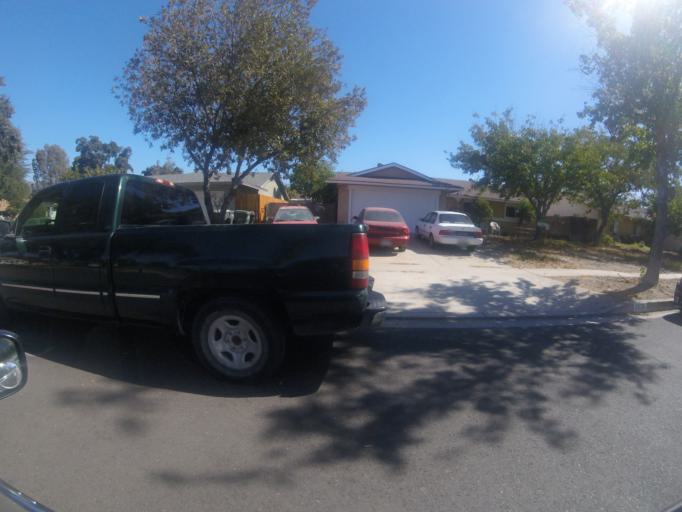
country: US
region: California
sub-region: San Bernardino County
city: Redlands
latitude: 34.0785
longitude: -117.1772
